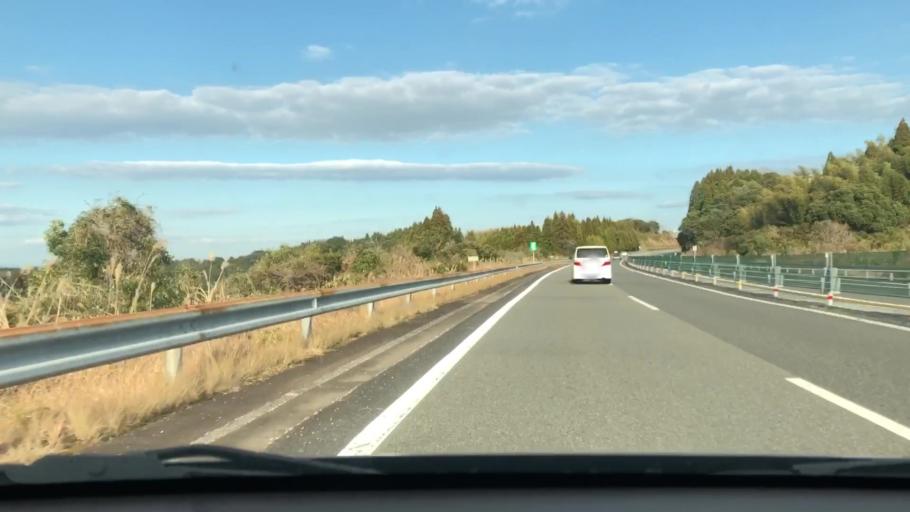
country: JP
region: Miyazaki
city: Miyazaki-shi
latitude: 31.8290
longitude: 131.3129
